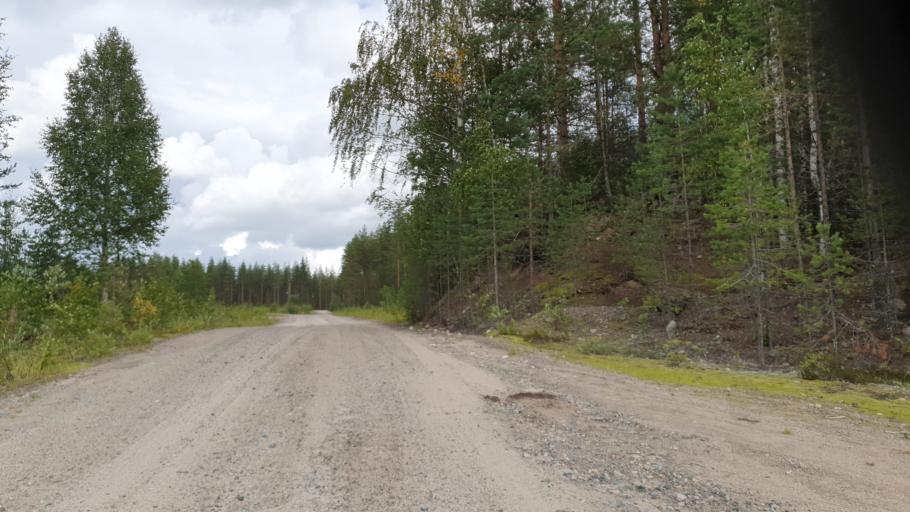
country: FI
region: Kainuu
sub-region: Kehys-Kainuu
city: Kuhmo
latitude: 64.1531
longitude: 29.3778
